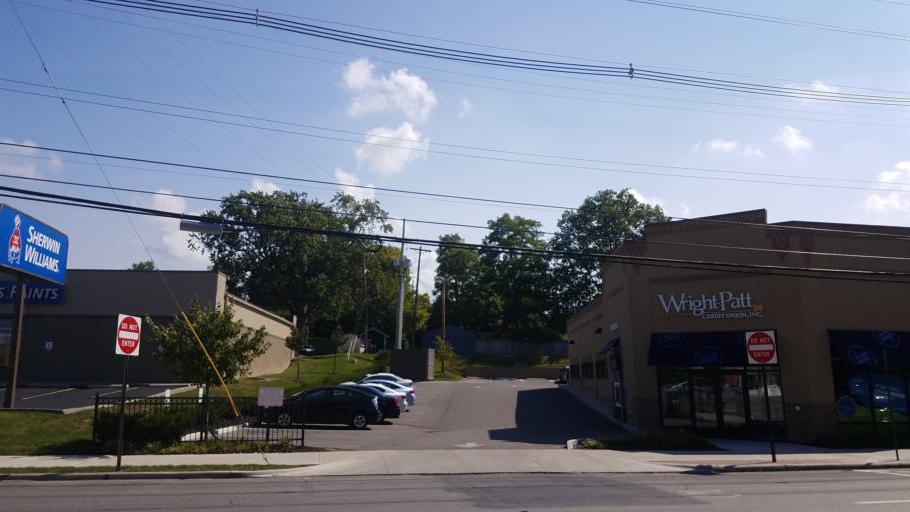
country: US
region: Ohio
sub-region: Franklin County
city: Grandview Heights
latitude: 40.0263
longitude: -83.0146
